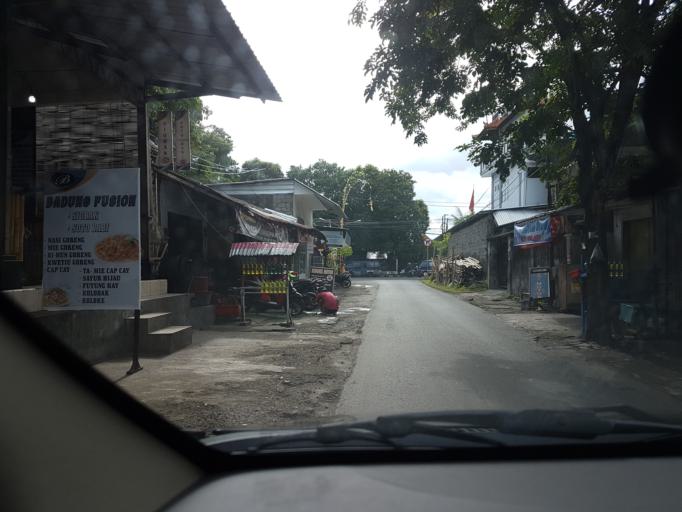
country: ID
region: Bali
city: Denpasar
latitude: -8.6624
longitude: 115.2078
